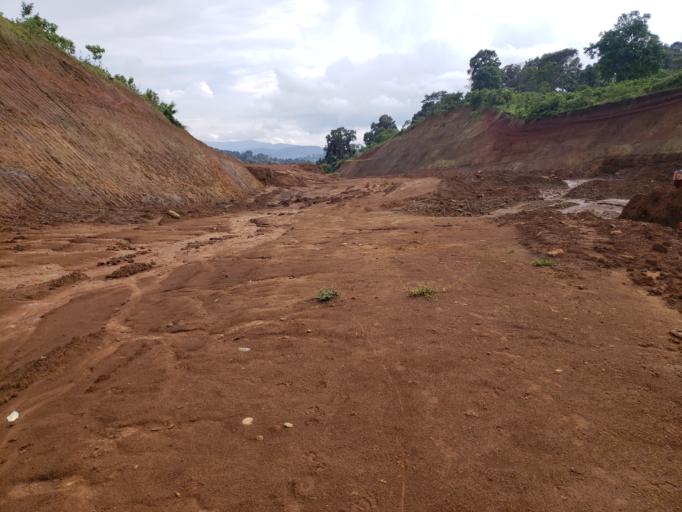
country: ET
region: Oromiya
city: Dodola
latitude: 6.5473
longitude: 39.4220
